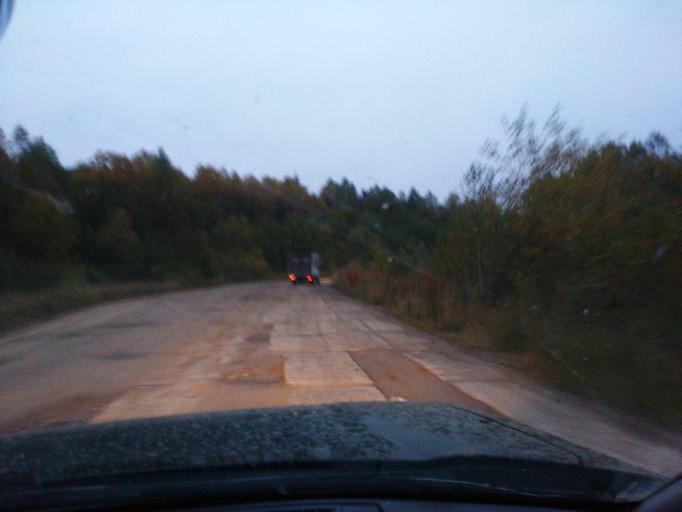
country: RU
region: Perm
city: Gornozavodsk
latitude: 57.8755
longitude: 58.4300
